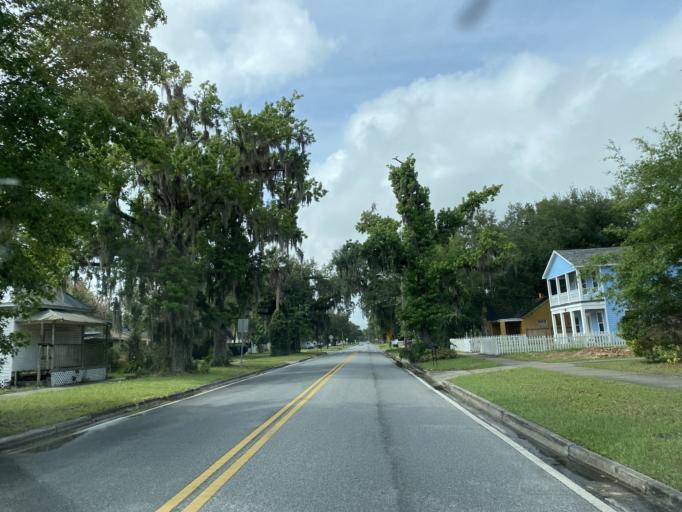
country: US
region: Florida
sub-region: Seminole County
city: Sanford
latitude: 28.8063
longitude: -81.2650
